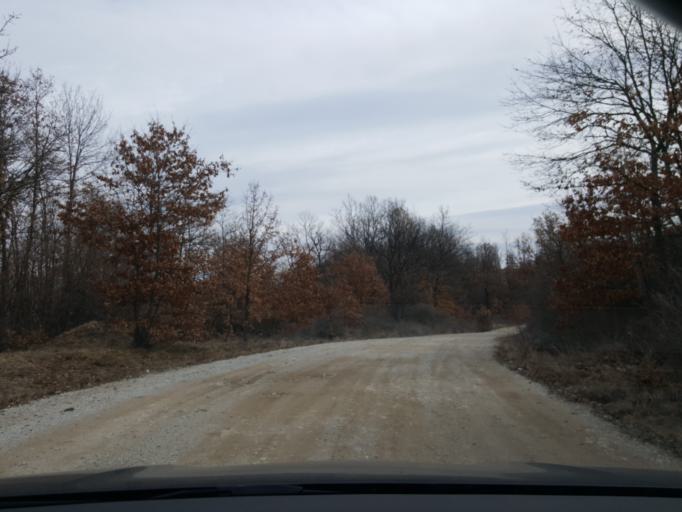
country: RS
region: Central Serbia
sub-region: Pirotski Okrug
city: Dimitrovgrad
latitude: 43.0017
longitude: 22.7499
